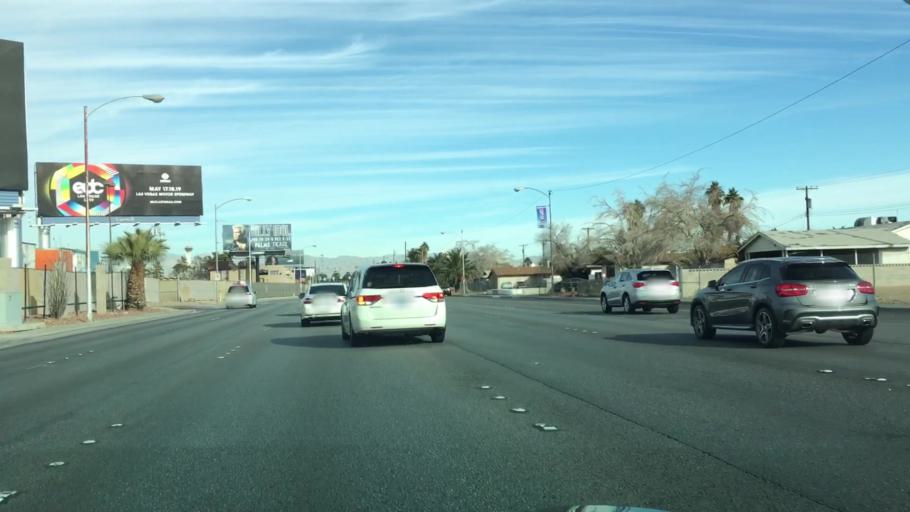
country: US
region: Nevada
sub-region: Clark County
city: Paradise
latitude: 36.0955
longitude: -115.1460
